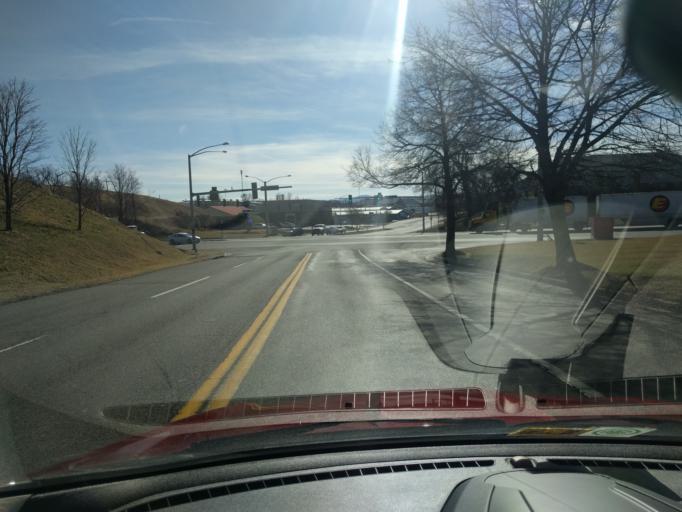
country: US
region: Virginia
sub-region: City of Roanoke
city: Roanoke
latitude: 37.2830
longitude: -79.9298
